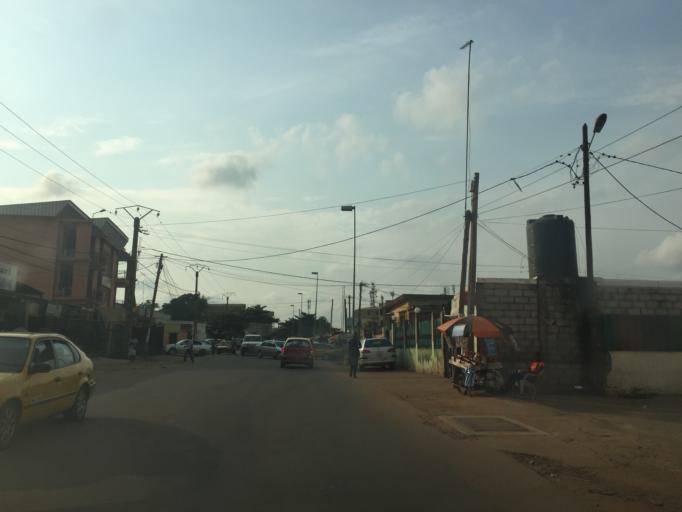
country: CM
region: Centre
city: Yaounde
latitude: 3.8797
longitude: 11.5241
